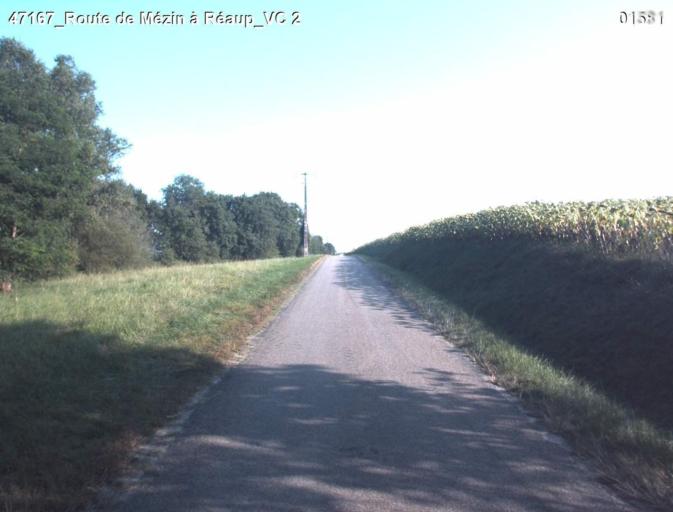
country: FR
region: Aquitaine
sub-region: Departement du Lot-et-Garonne
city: Mezin
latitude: 44.0713
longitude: 0.2548
